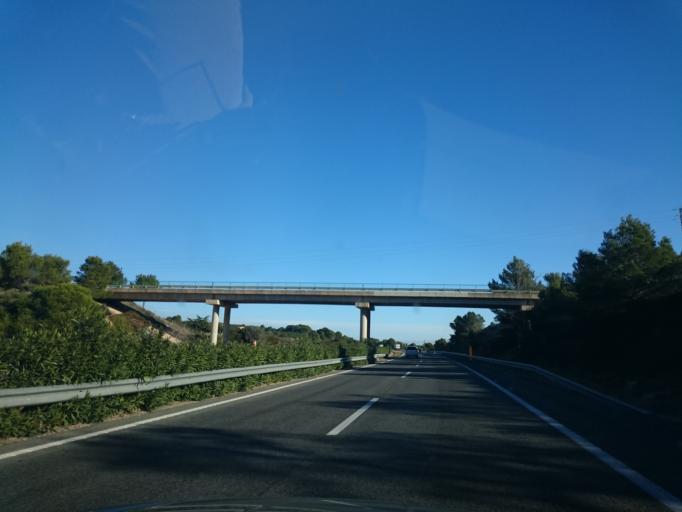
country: ES
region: Catalonia
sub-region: Provincia de Tarragona
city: L'Ampolla
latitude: 40.8299
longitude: 0.7360
